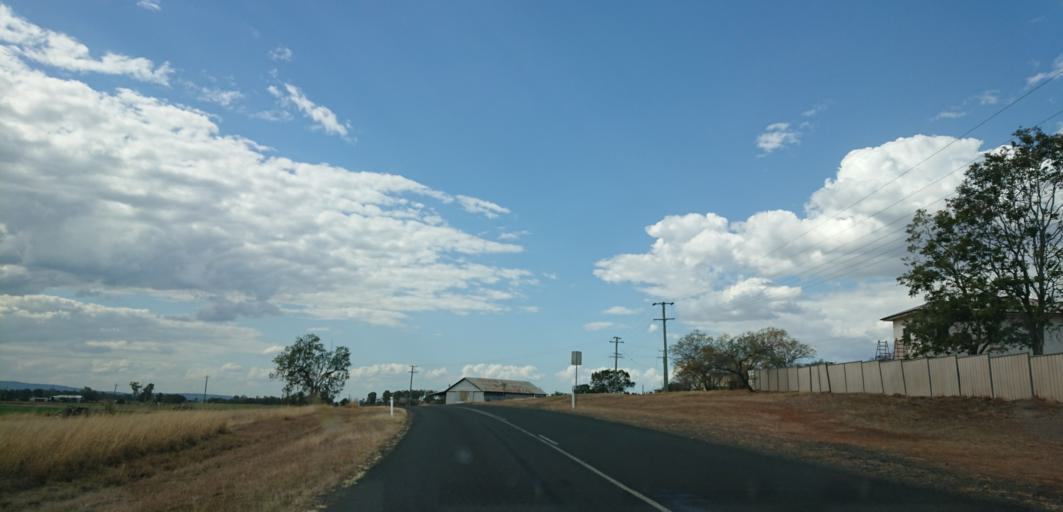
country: AU
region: Queensland
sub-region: Lockyer Valley
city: Gatton
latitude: -27.6203
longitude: 152.2062
